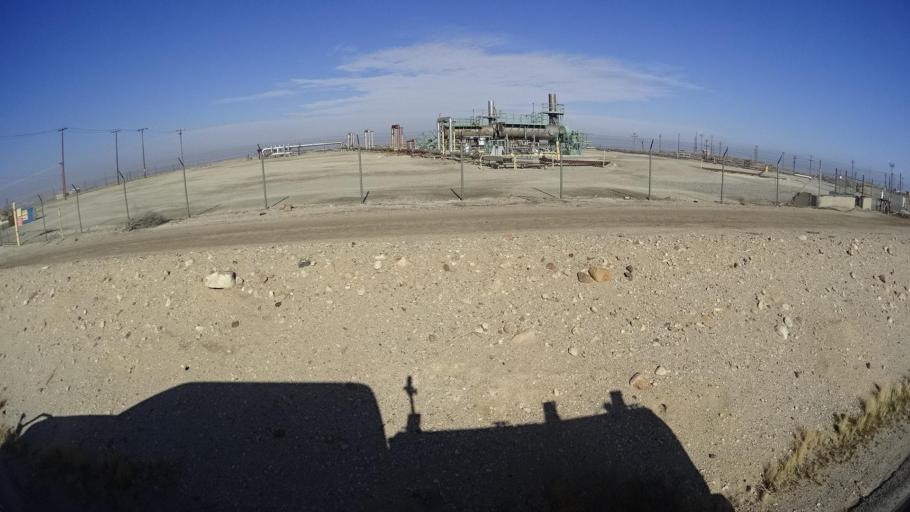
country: US
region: California
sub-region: Kern County
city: Taft Heights
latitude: 35.1134
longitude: -119.4720
